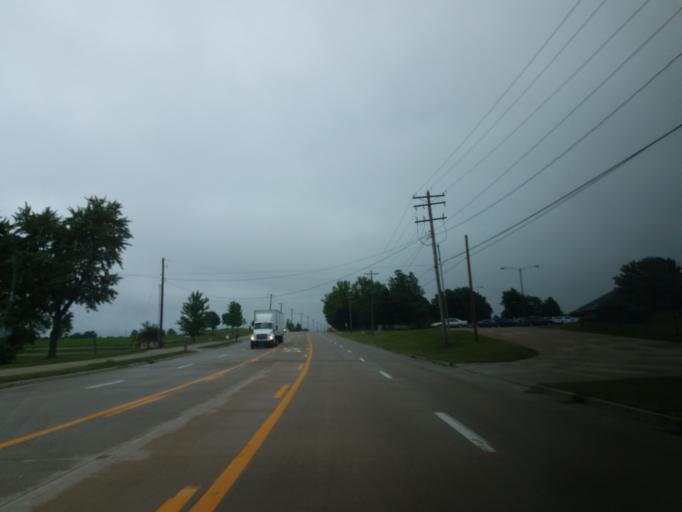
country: US
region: Illinois
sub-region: McLean County
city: Bloomington
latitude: 40.4497
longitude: -89.0020
